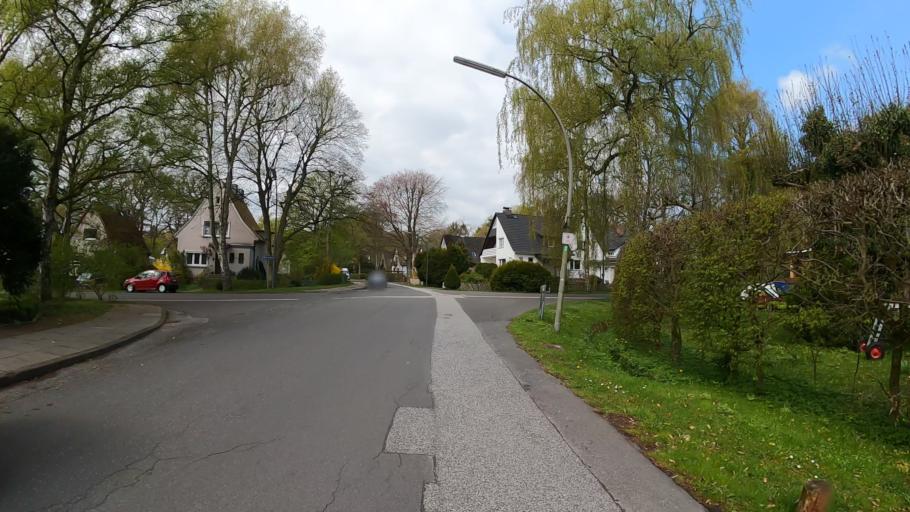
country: DE
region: Hamburg
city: Stellingen
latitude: 53.6129
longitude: 9.9494
